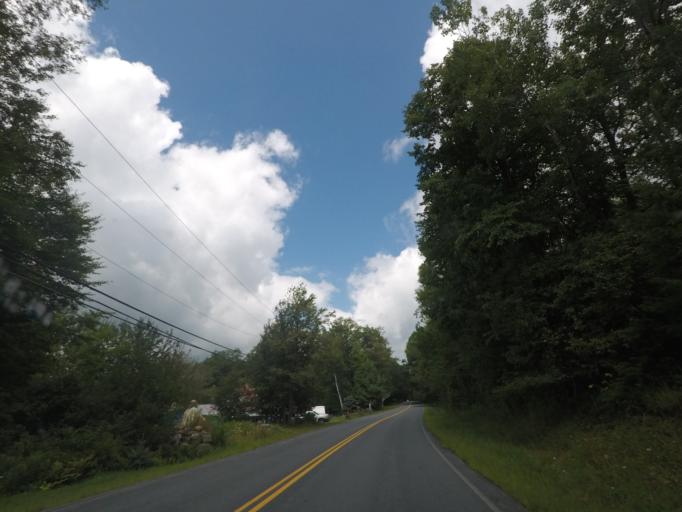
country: US
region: New York
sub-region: Rensselaer County
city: Averill Park
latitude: 42.6466
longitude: -73.4942
